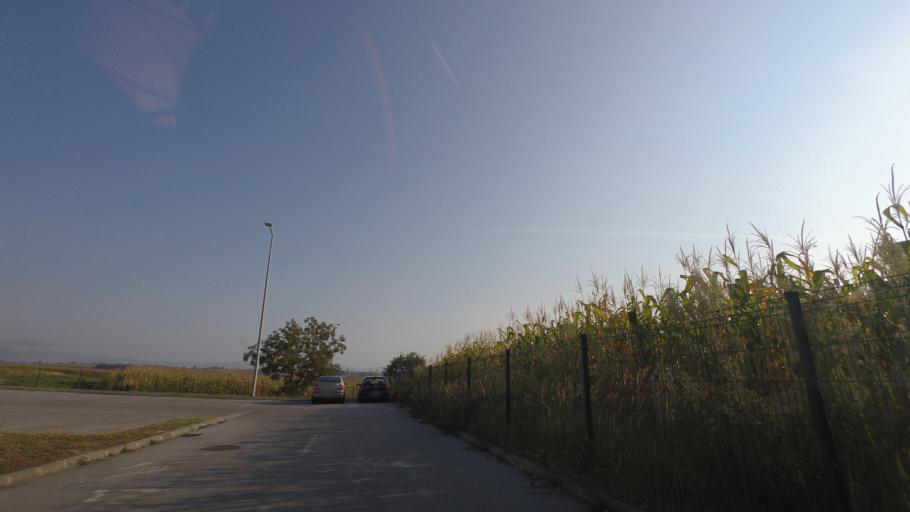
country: HR
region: Pozesko-Slavonska
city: Pozega
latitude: 45.3444
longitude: 17.7014
